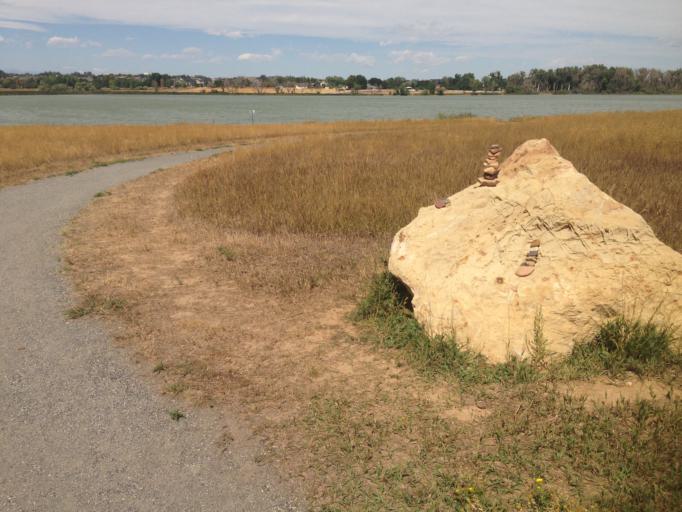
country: US
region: Colorado
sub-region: Adams County
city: Northglenn
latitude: 39.9501
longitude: -105.0117
